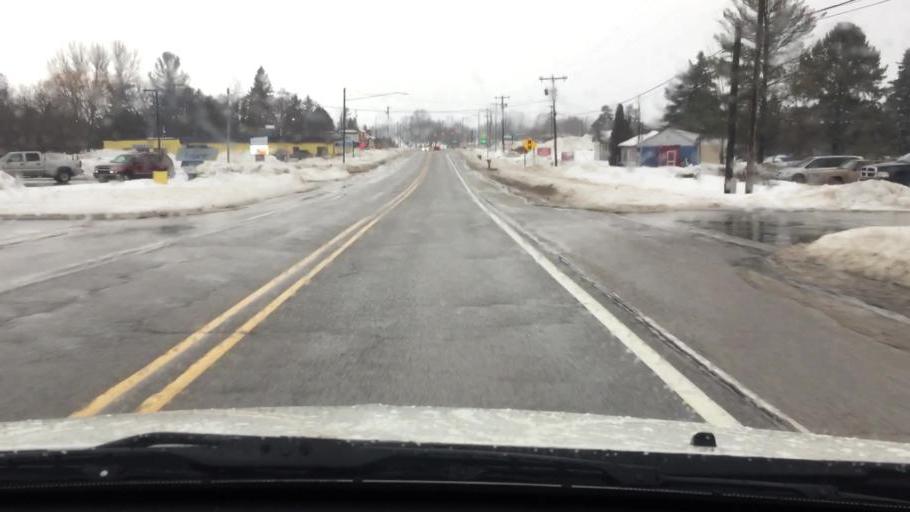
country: US
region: Michigan
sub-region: Charlevoix County
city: East Jordan
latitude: 45.1513
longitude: -85.1399
